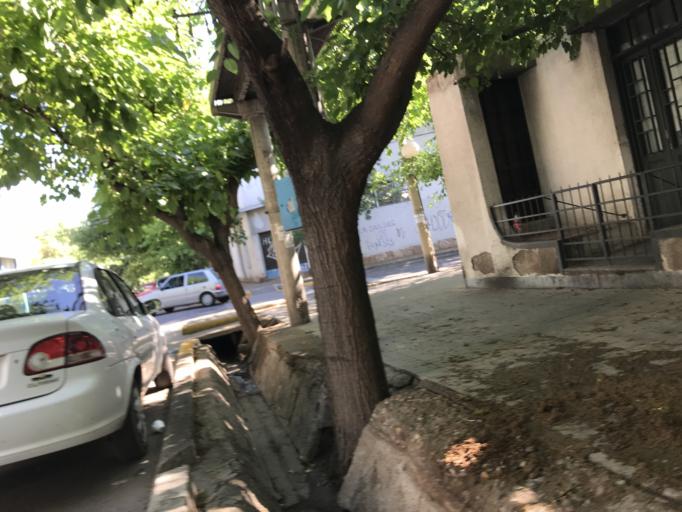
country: AR
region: Mendoza
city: Mendoza
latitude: -32.8816
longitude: -68.8310
